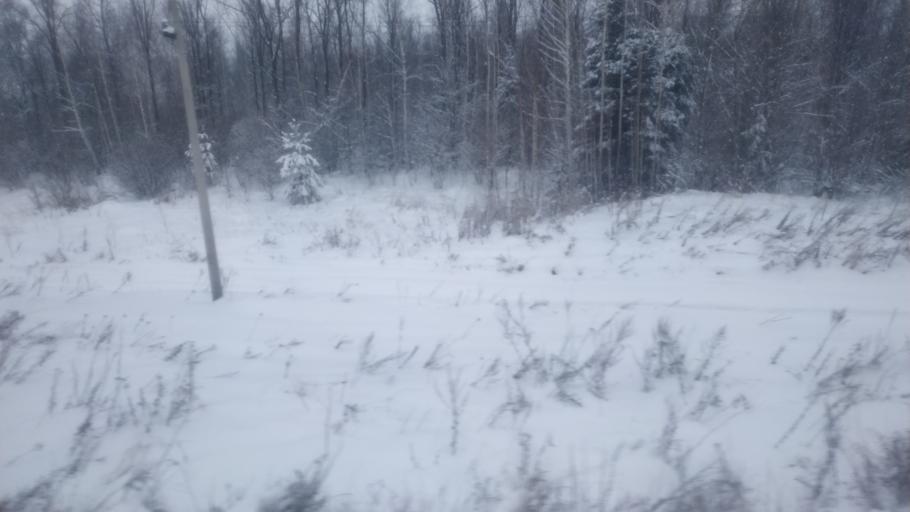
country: RU
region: Udmurtiya
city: Kiyasovo
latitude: 56.5013
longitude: 53.3678
